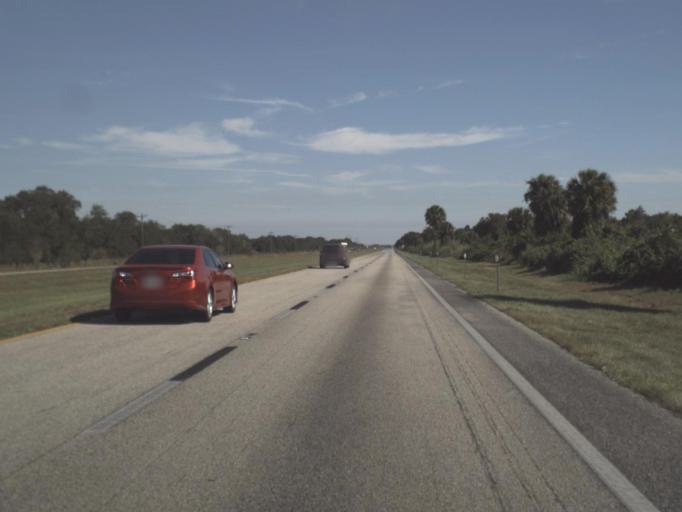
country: US
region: Florida
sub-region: Hendry County
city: Port LaBelle
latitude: 26.9213
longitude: -81.3026
